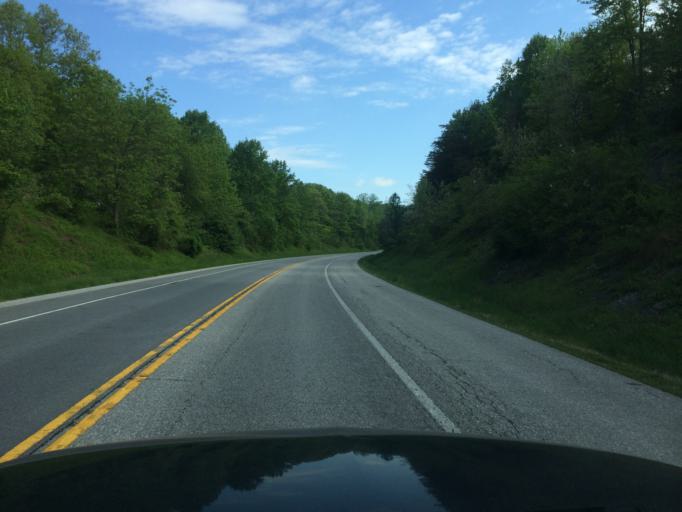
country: US
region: Maryland
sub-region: Carroll County
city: Westminster
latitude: 39.5135
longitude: -76.9945
